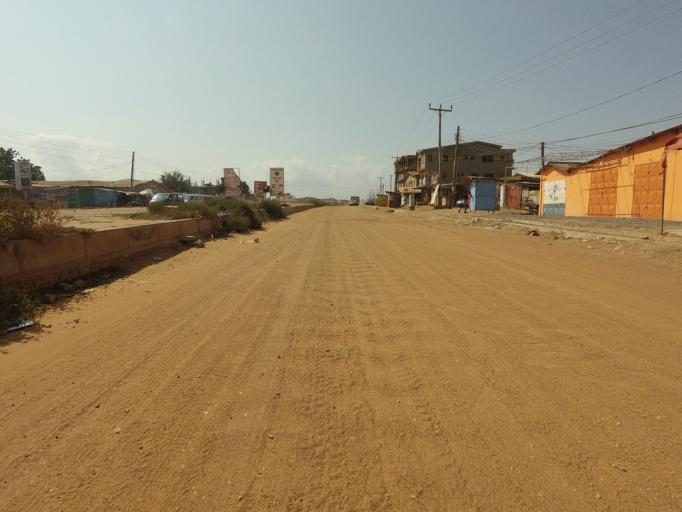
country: GH
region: Greater Accra
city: Teshi Old Town
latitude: 5.6127
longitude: -0.1240
